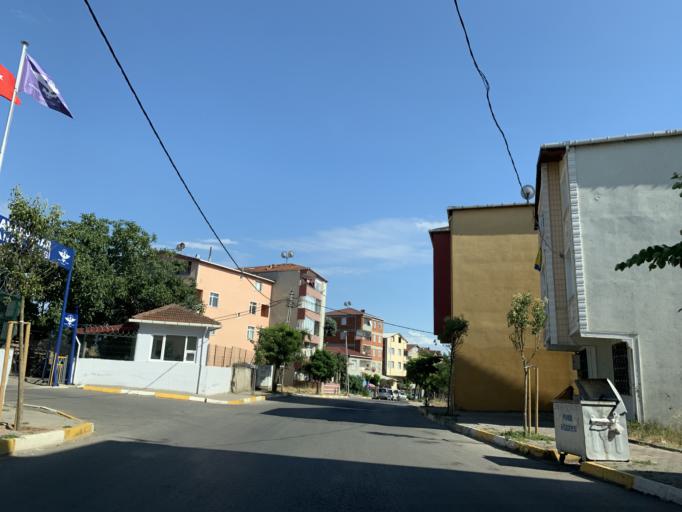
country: TR
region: Istanbul
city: Pendik
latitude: 40.8856
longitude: 29.2787
